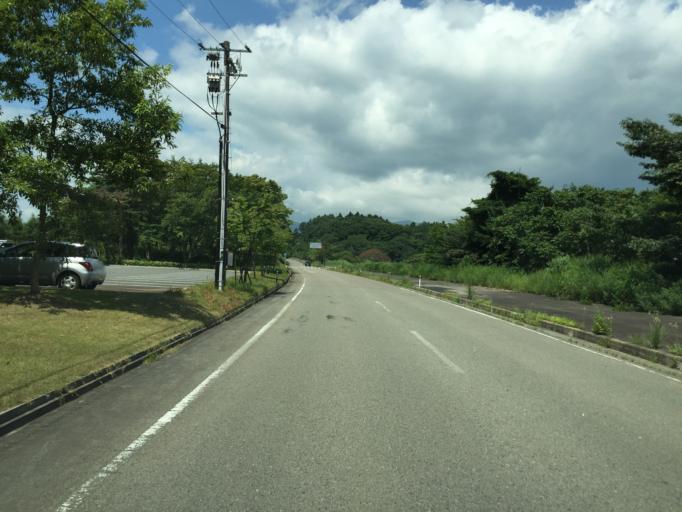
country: JP
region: Fukushima
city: Inawashiro
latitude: 37.5131
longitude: 140.0197
